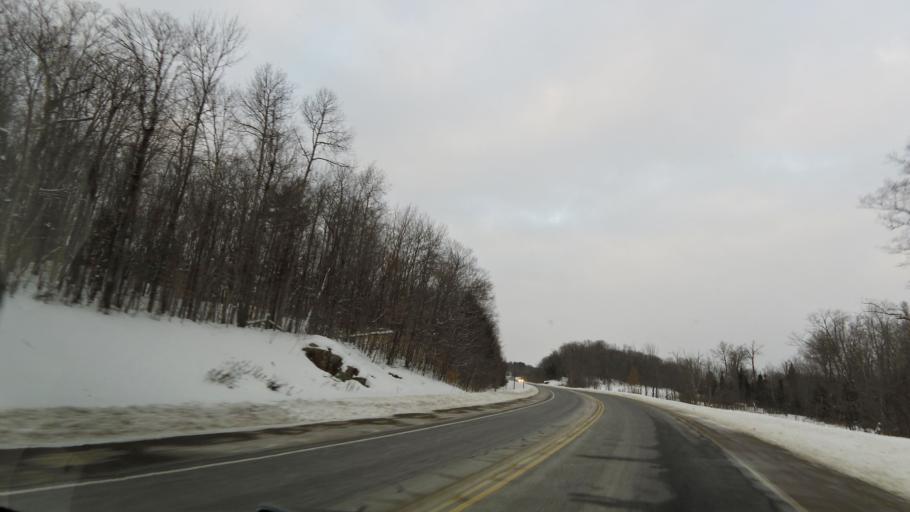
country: CA
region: Ontario
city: Omemee
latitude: 44.8062
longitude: -78.7988
